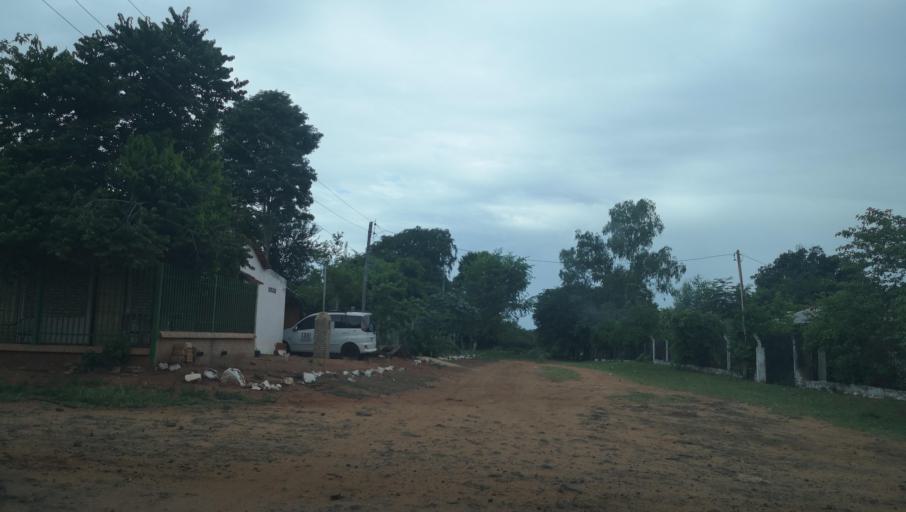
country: PY
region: San Pedro
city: Capiibary
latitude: -24.7279
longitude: -56.0137
